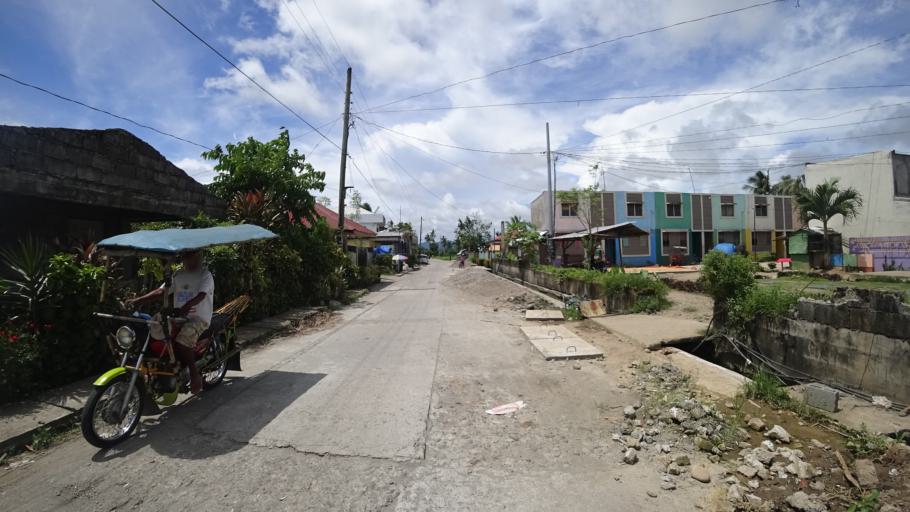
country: PH
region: Eastern Visayas
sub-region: Province of Leyte
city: Alangalang
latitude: 11.2094
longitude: 124.8449
